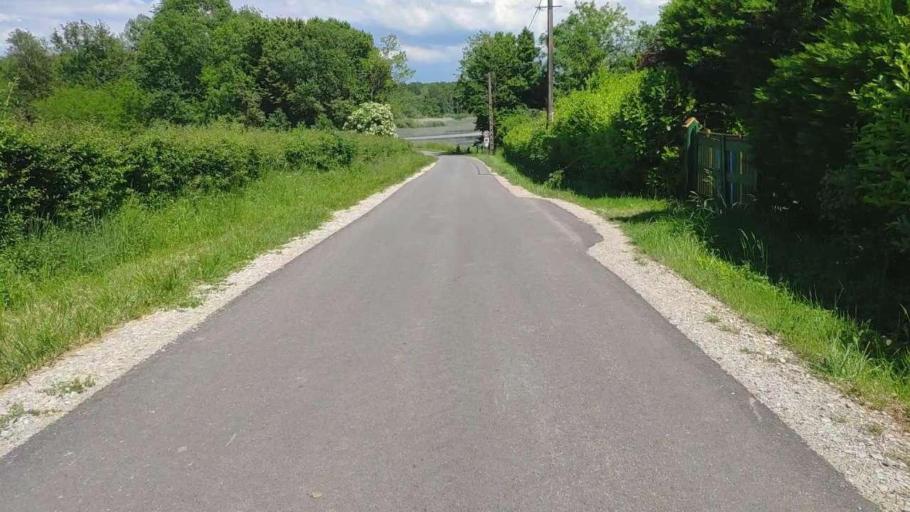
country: FR
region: Franche-Comte
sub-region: Departement du Jura
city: Bletterans
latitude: 46.7828
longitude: 5.3917
